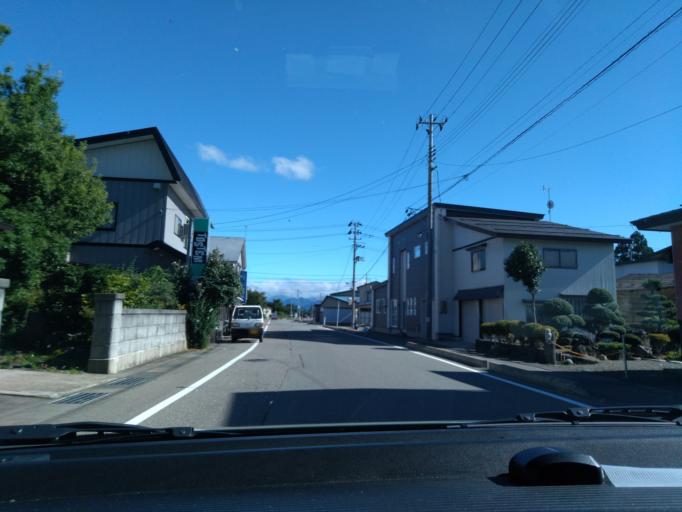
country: JP
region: Akita
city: Yuzawa
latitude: 39.2030
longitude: 140.5513
